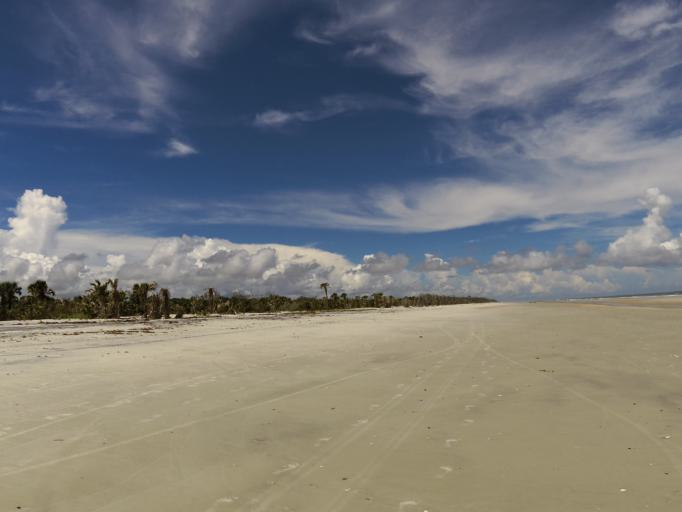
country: US
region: Florida
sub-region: Duval County
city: Atlantic Beach
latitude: 30.4671
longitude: -81.4120
